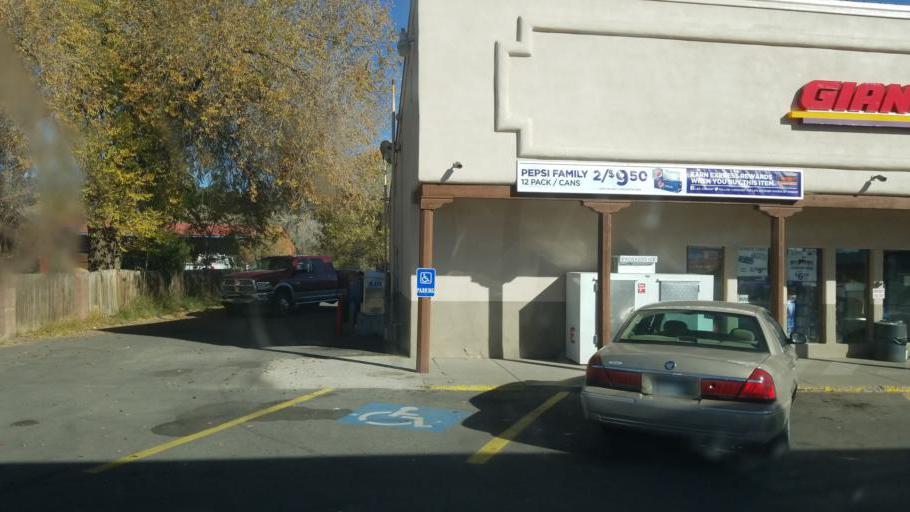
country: US
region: New Mexico
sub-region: Rio Arriba County
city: Chama
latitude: 36.8830
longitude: -106.5843
